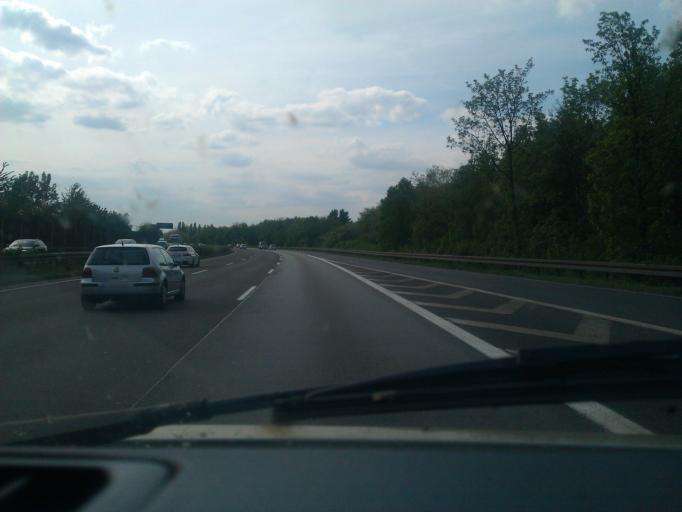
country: DE
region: North Rhine-Westphalia
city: Meiderich
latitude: 51.4796
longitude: 6.7007
